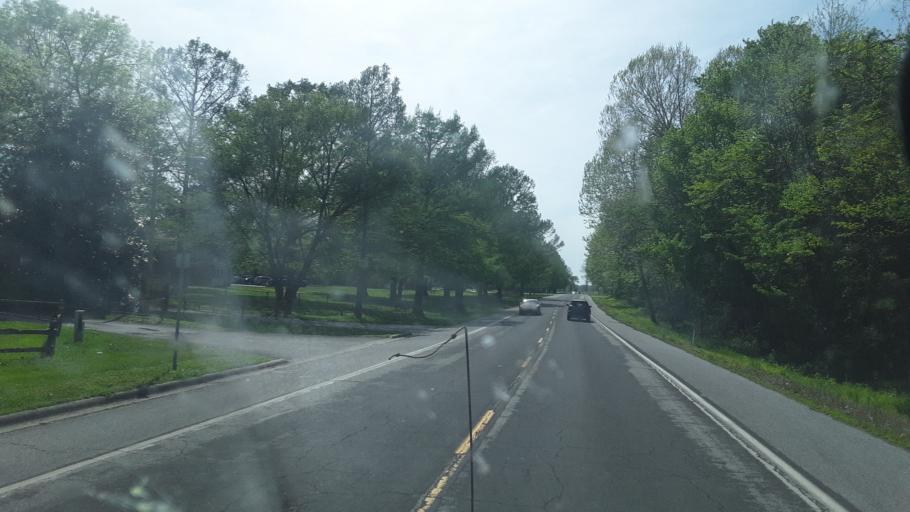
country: US
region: Illinois
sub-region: Jackson County
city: Carbondale
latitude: 37.7008
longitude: -89.2323
